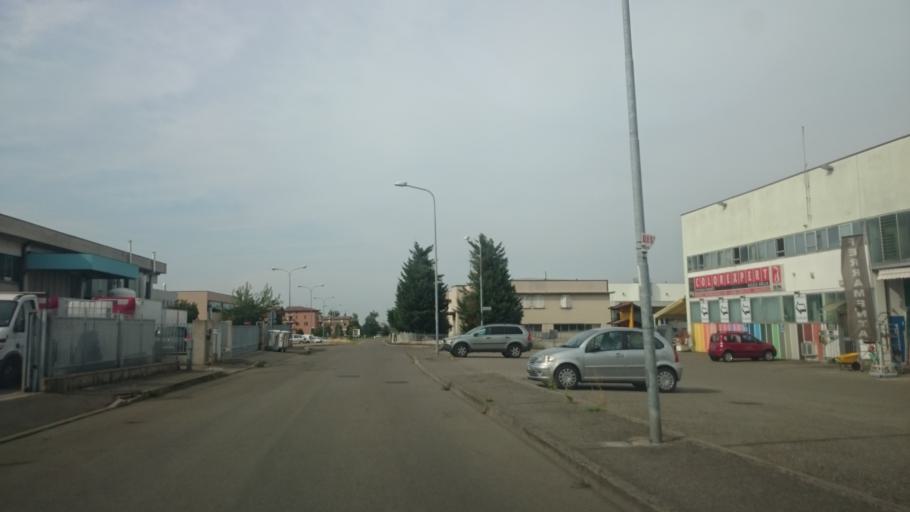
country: IT
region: Emilia-Romagna
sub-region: Provincia di Reggio Emilia
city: Forche
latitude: 44.6696
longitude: 10.5975
